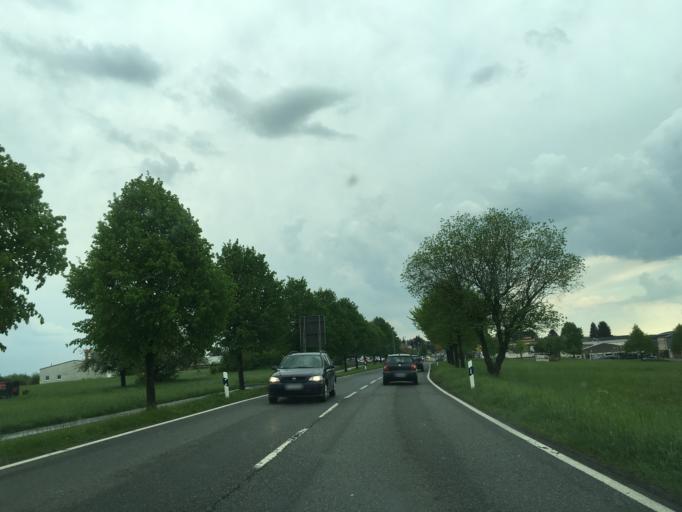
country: DE
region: Rheinland-Pfalz
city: Oberraden
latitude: 50.5448
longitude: 7.5231
